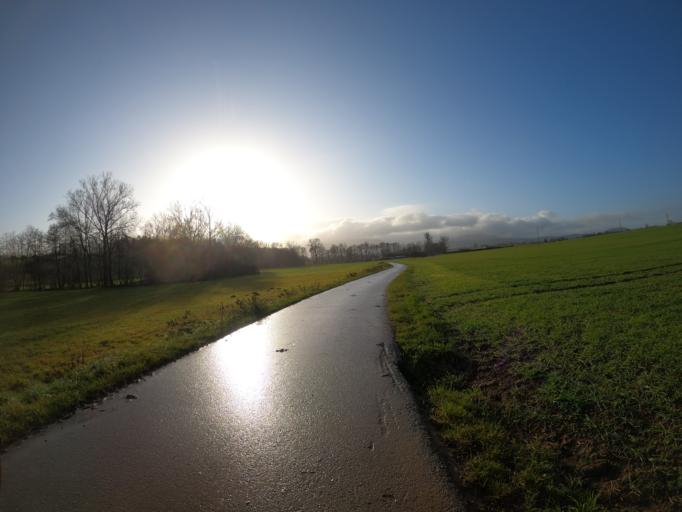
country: DE
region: Baden-Wuerttemberg
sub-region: Regierungsbezirk Stuttgart
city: Heiningen
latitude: 48.6693
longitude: 9.6248
